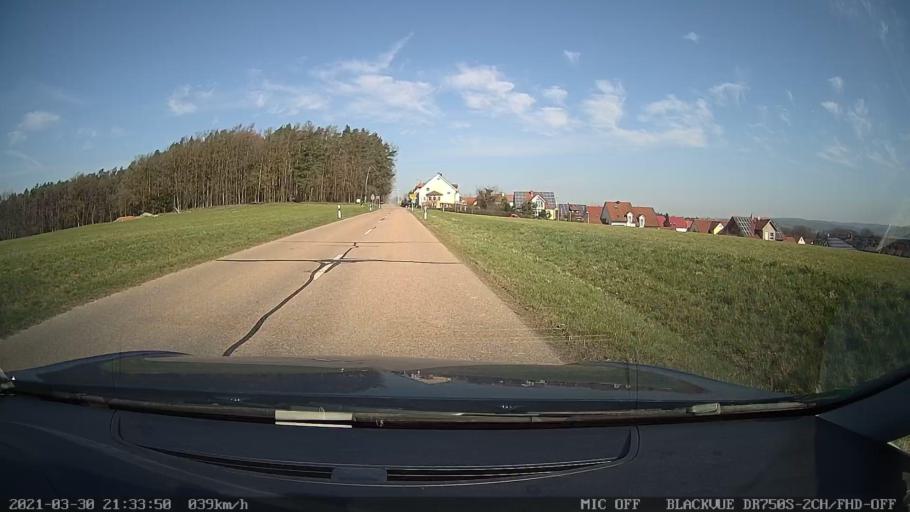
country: DE
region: Bavaria
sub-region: Upper Palatinate
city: Zeitlarn
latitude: 49.0947
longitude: 12.1022
